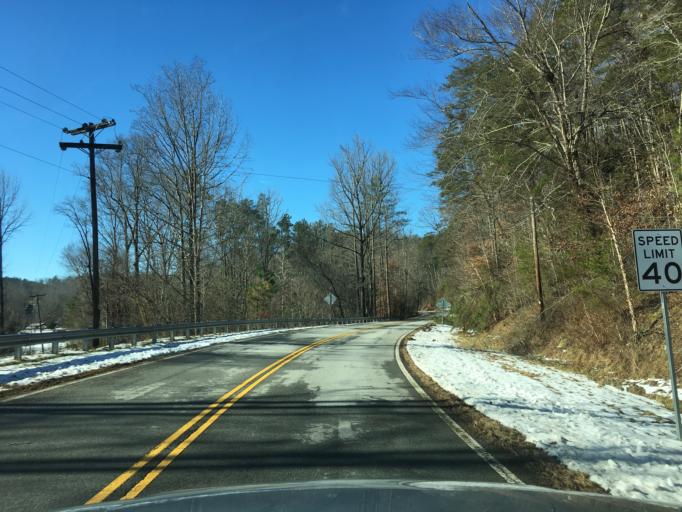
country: US
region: South Carolina
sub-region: Greenville County
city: Slater-Marietta
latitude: 35.0715
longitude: -82.6073
